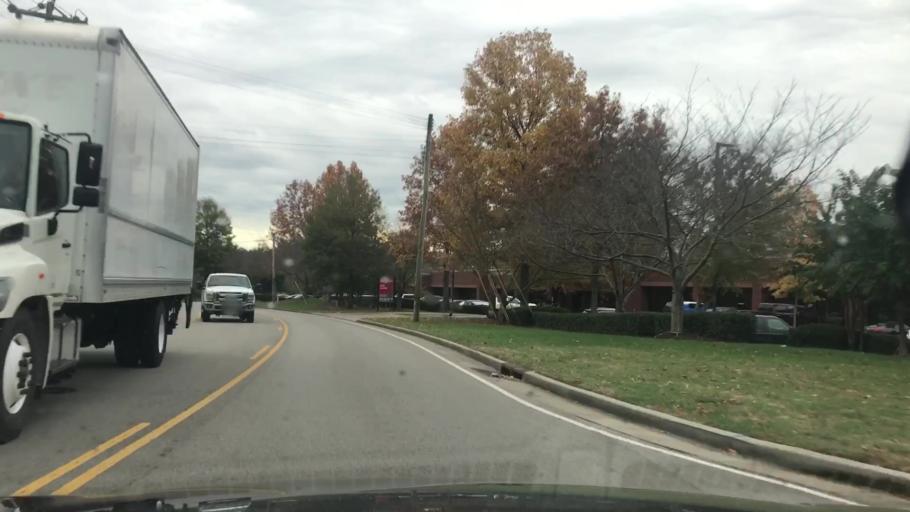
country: US
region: Tennessee
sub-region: Williamson County
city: Franklin
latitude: 35.9536
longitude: -86.8226
